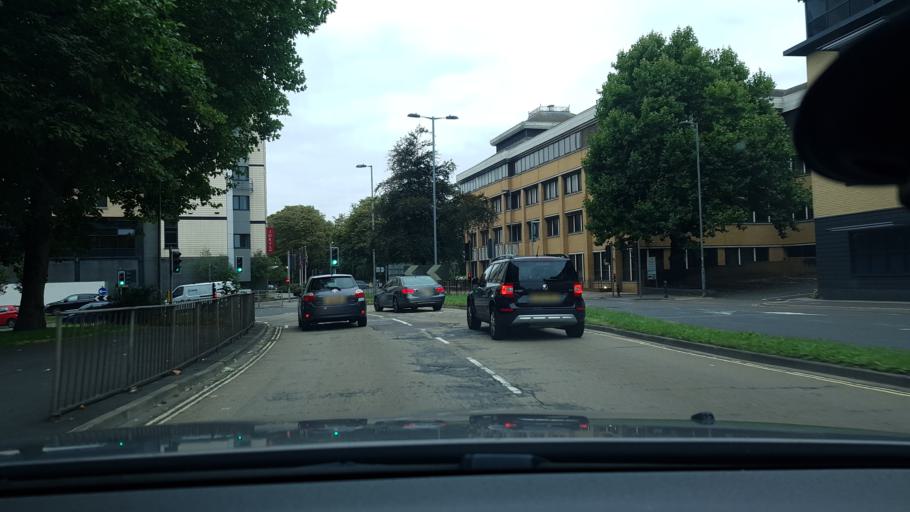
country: GB
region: England
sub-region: Southampton
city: Southampton
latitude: 50.9117
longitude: -1.4012
